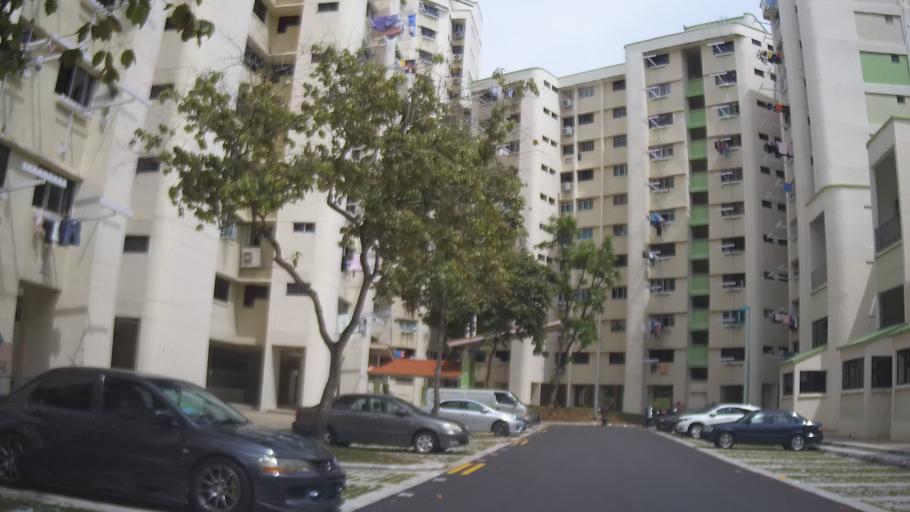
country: SG
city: Singapore
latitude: 1.3496
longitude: 103.8865
